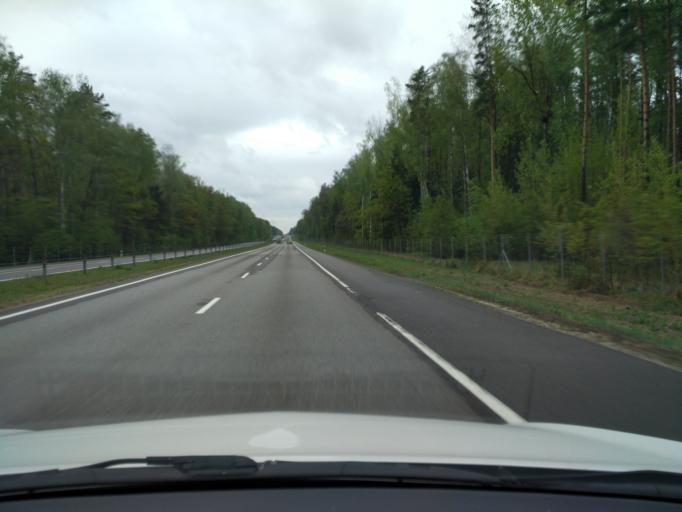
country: BY
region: Mogilev
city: Asipovichy
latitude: 53.3538
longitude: 28.6235
